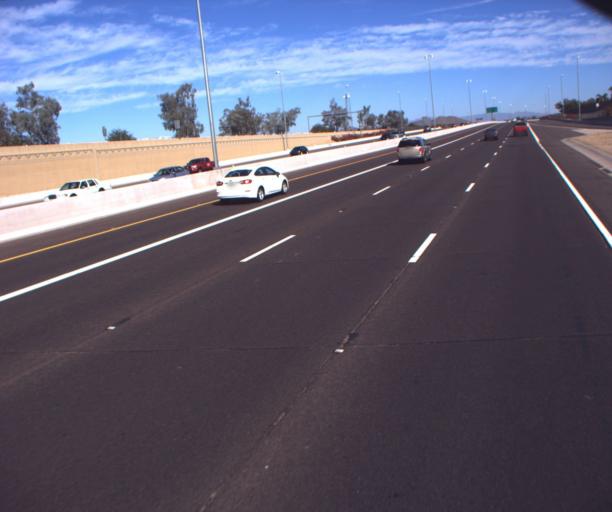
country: US
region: Arizona
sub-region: Maricopa County
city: Sun City
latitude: 33.6538
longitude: -112.2322
